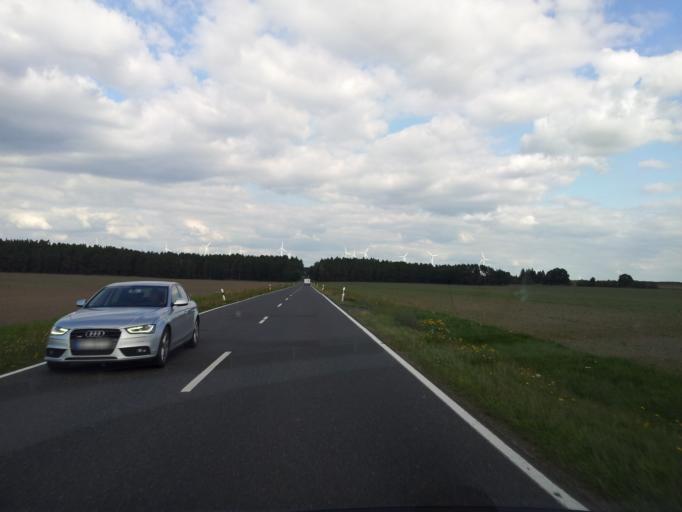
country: DE
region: Brandenburg
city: Sallgast
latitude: 51.6065
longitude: 13.7958
